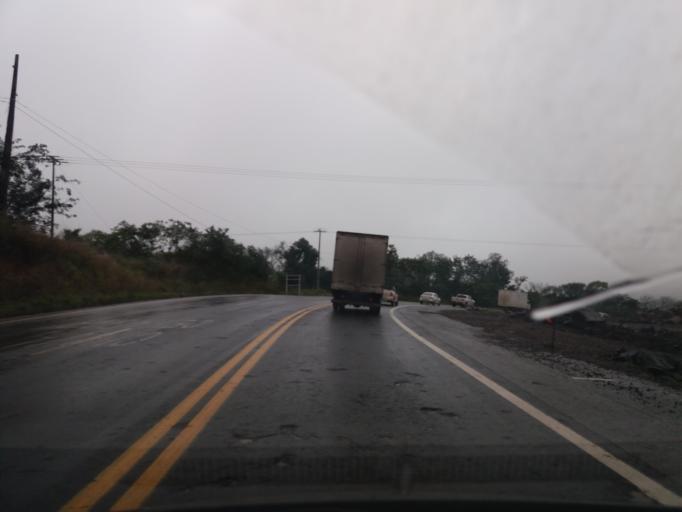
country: BR
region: Parana
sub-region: Realeza
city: Realeza
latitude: -25.4725
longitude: -53.5873
